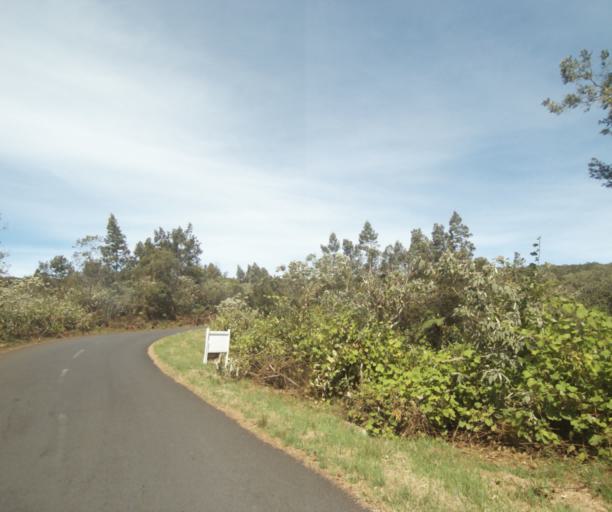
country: RE
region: Reunion
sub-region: Reunion
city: Trois-Bassins
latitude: -21.0536
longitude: 55.3532
